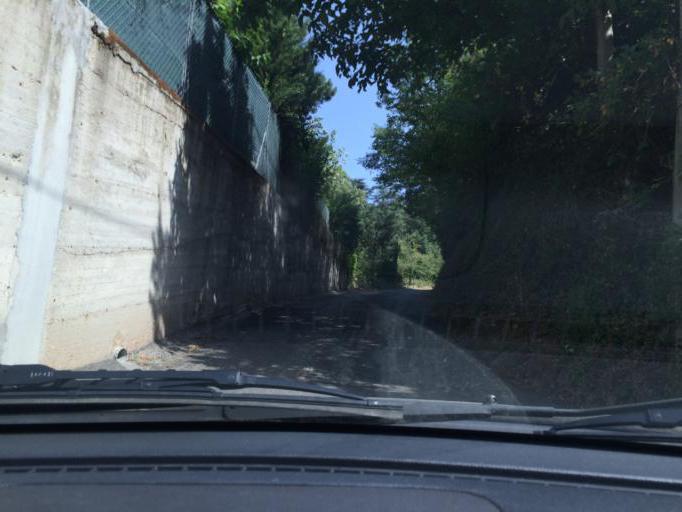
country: FR
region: Rhone-Alpes
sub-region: Departement du Rhone
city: Limonest
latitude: 45.8313
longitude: 4.7828
